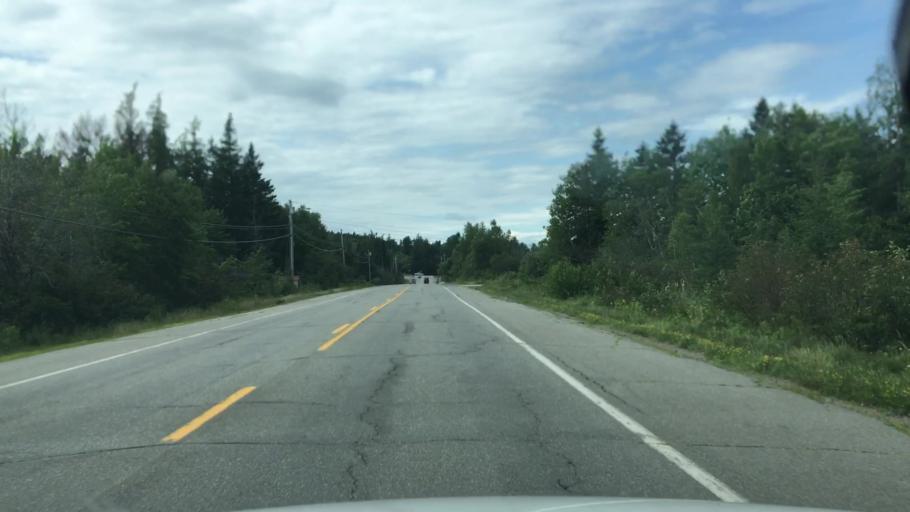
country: US
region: Maine
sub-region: Washington County
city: Eastport
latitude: 44.9677
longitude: -67.0697
